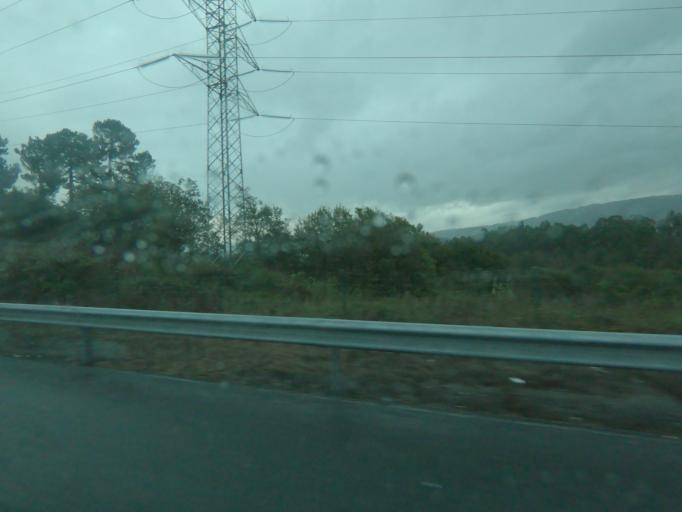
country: ES
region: Galicia
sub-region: Provincia de Pontevedra
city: Pontevedra
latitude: 42.3991
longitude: -8.6485
